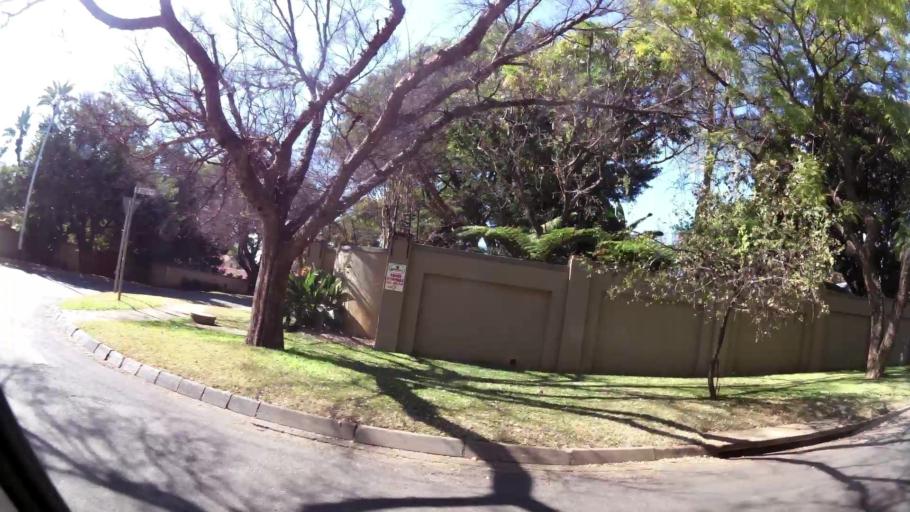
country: ZA
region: Gauteng
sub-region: City of Tshwane Metropolitan Municipality
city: Pretoria
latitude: -25.7758
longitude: 28.2488
